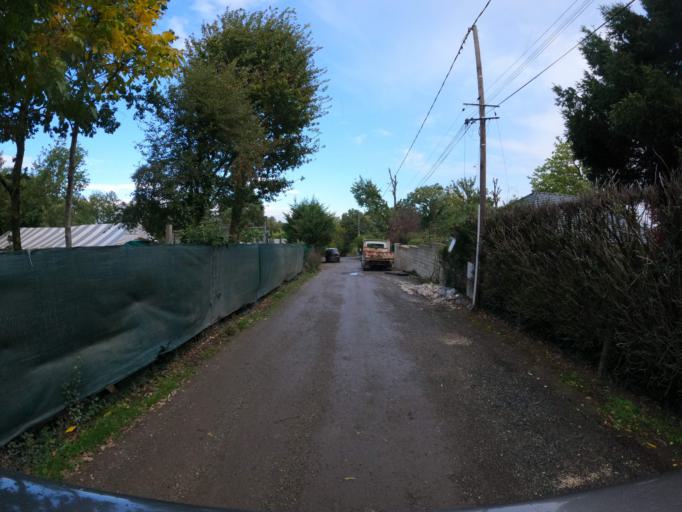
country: FR
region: Ile-de-France
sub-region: Departement de Seine-et-Marne
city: Saint-Germain-sur-Morin
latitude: 48.8733
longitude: 2.8537
